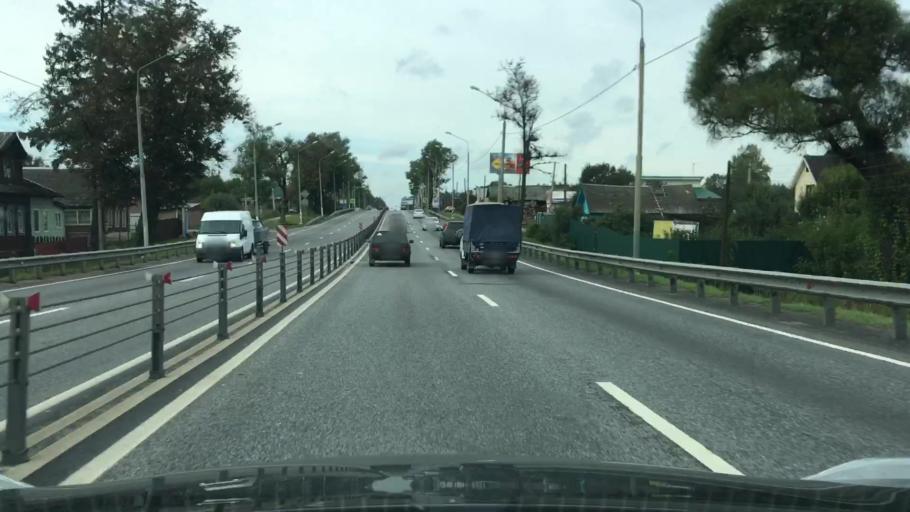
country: RU
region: Tverskaya
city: Zavidovo
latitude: 56.5497
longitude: 36.5152
